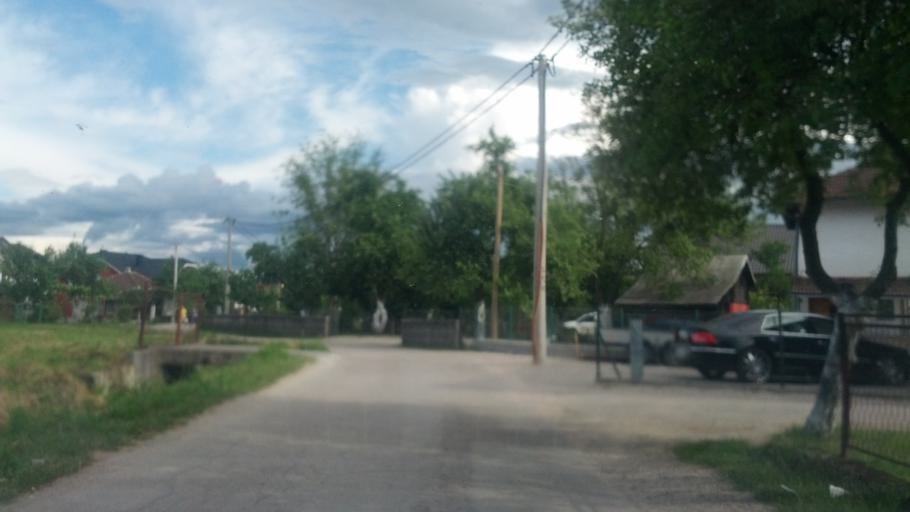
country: BA
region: Federation of Bosnia and Herzegovina
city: Bihac
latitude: 44.8409
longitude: 15.8749
